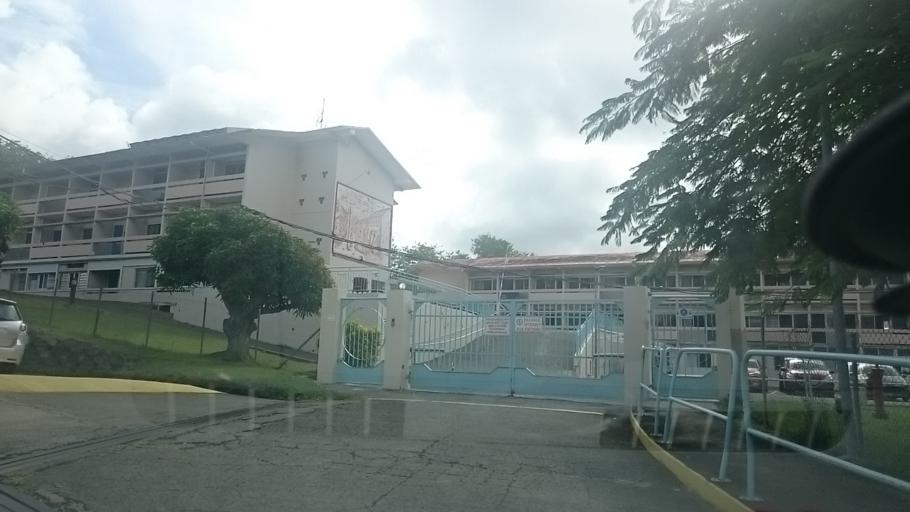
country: MQ
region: Martinique
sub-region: Martinique
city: Le Francois
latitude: 14.6076
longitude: -60.8972
